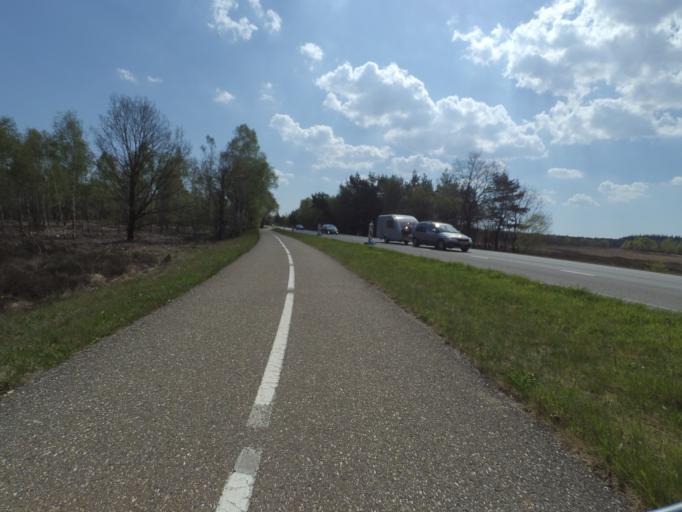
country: NL
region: Gelderland
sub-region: Gemeente Barneveld
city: Garderen
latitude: 52.2835
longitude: 5.6933
